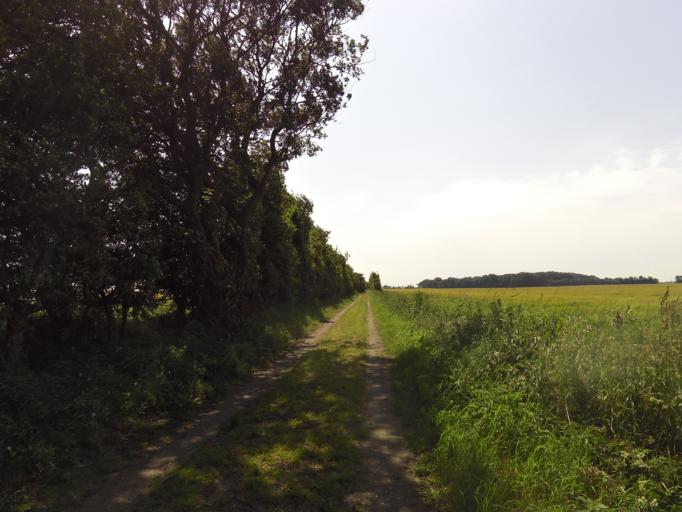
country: DK
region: South Denmark
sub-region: Aabenraa Kommune
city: Rodekro
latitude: 55.1515
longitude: 9.2475
